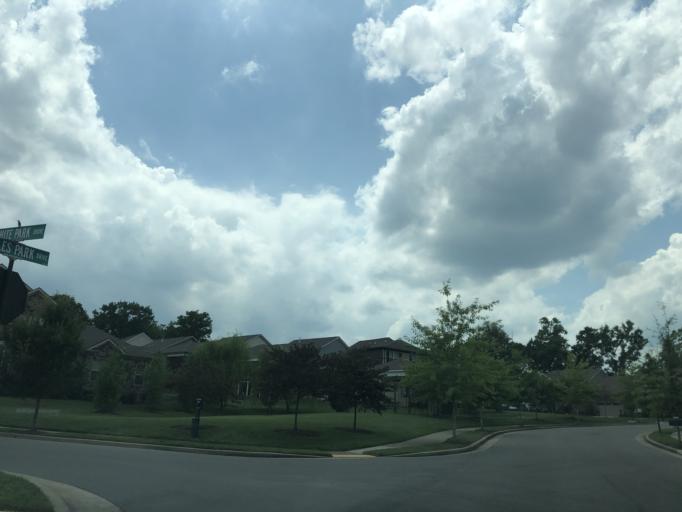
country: US
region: Tennessee
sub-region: Williamson County
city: Brentwood Estates
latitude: 36.0254
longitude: -86.7380
